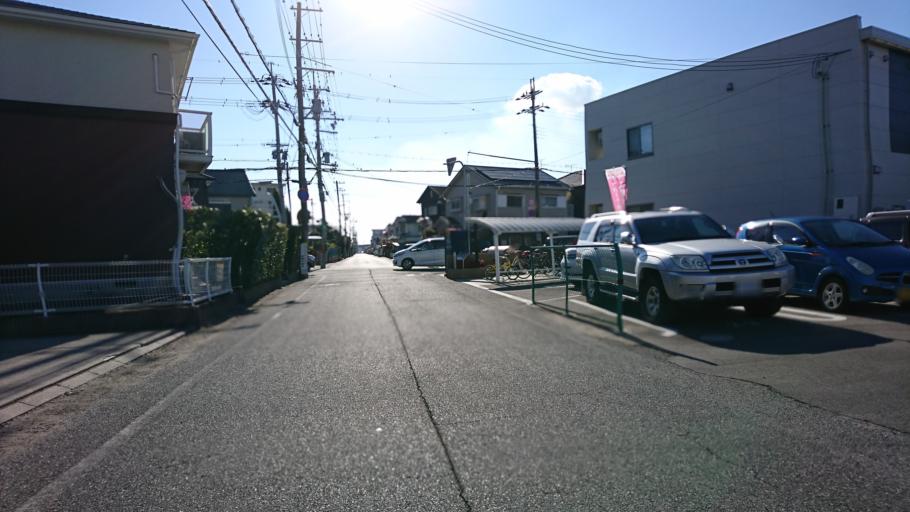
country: JP
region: Hyogo
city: Kakogawacho-honmachi
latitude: 34.7426
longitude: 134.8398
